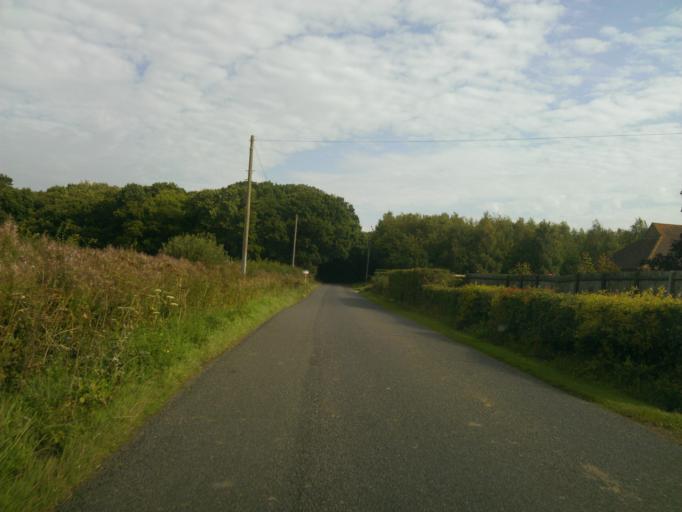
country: GB
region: England
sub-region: Essex
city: Saint Osyth
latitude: 51.8315
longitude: 1.1031
